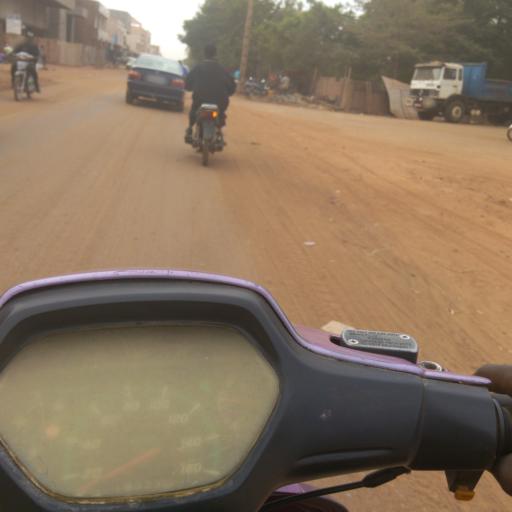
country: ML
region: Bamako
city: Bamako
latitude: 12.6647
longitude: -7.9358
